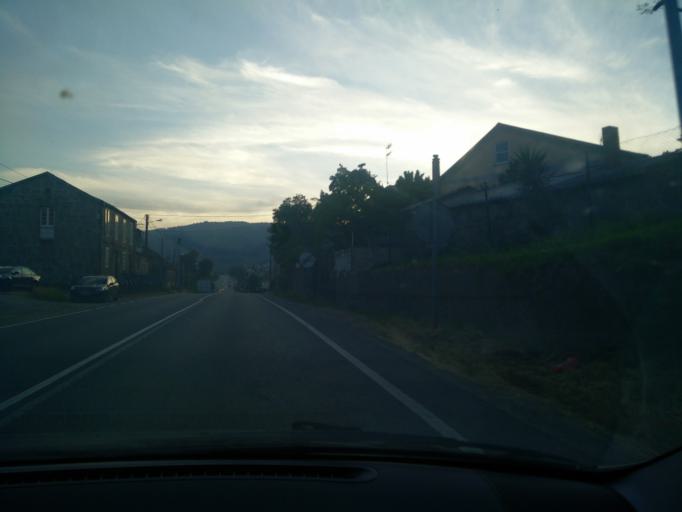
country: ES
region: Galicia
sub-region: Provincia de Pontevedra
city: Ponteareas
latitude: 42.1796
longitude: -8.5515
